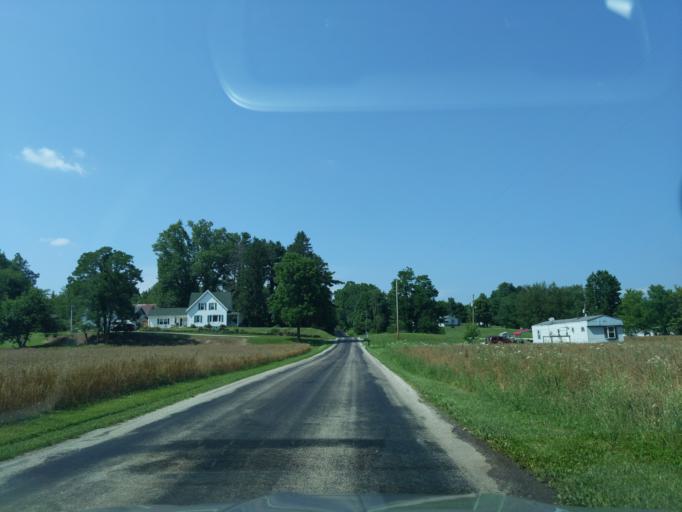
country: US
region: Indiana
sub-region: Ripley County
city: Osgood
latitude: 39.1121
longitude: -85.3436
